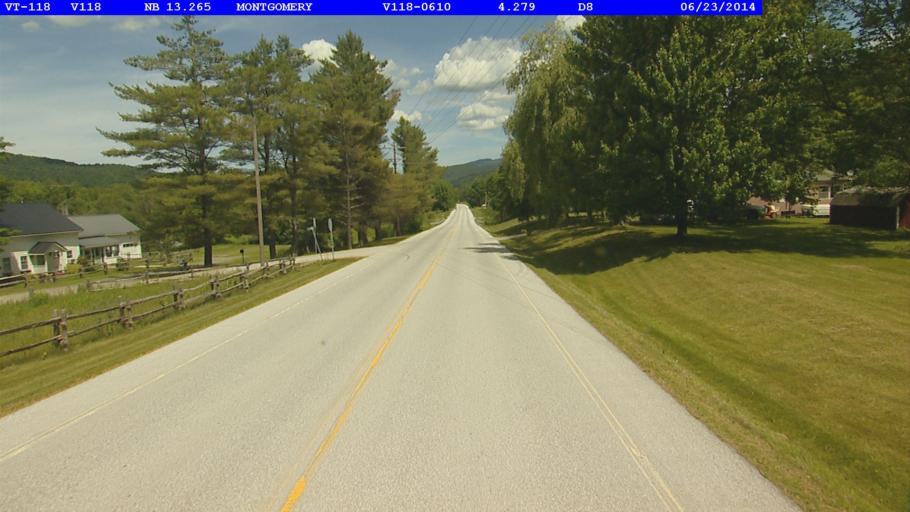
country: US
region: Vermont
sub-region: Franklin County
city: Richford
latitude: 44.8592
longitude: -72.6097
